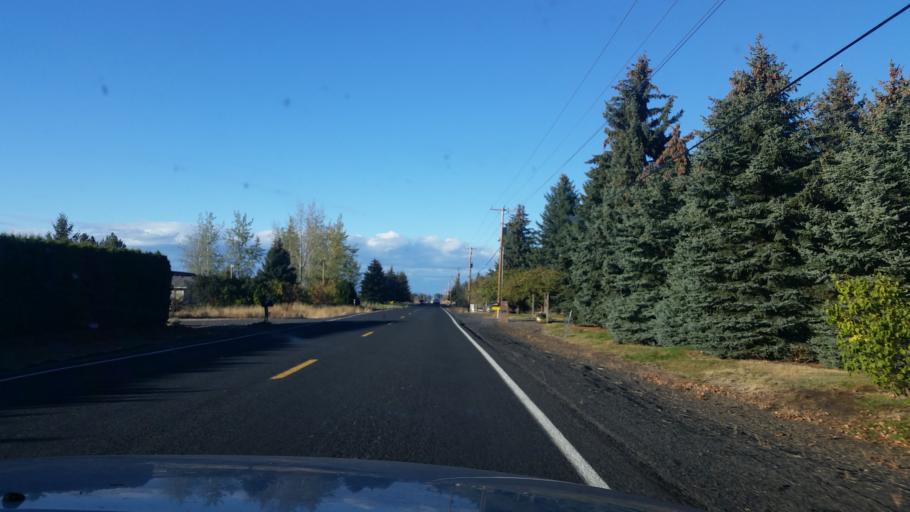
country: US
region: Washington
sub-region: Spokane County
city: Fairchild Air Force Base
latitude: 47.5878
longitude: -117.6075
